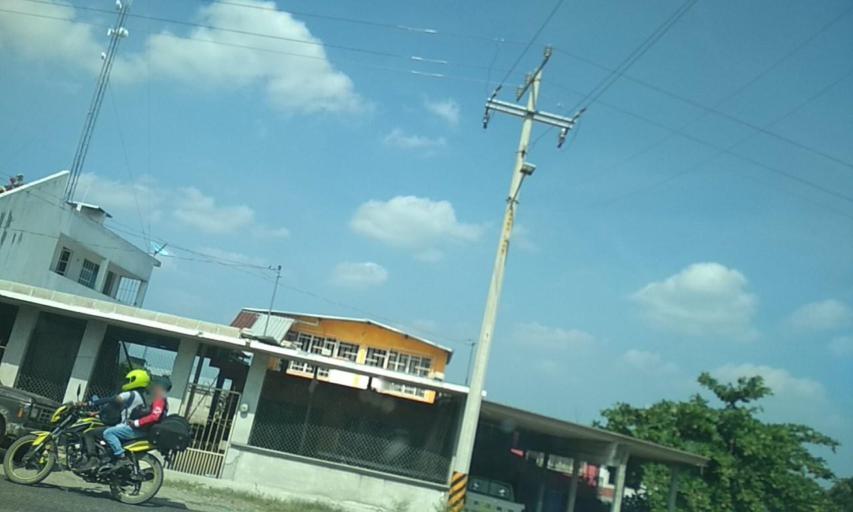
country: MX
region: Veracruz
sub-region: Atzalan
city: Colonias Pedernales
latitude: 20.0550
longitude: -97.0190
